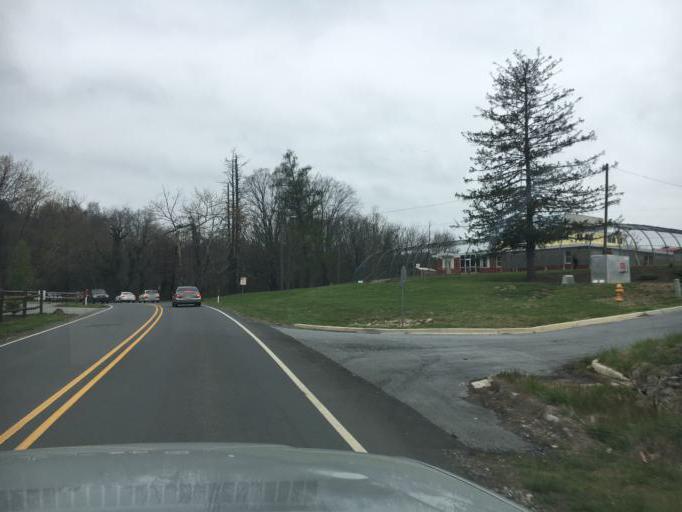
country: US
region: North Carolina
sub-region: Buncombe County
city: Woodfin
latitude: 35.6149
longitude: -82.6270
